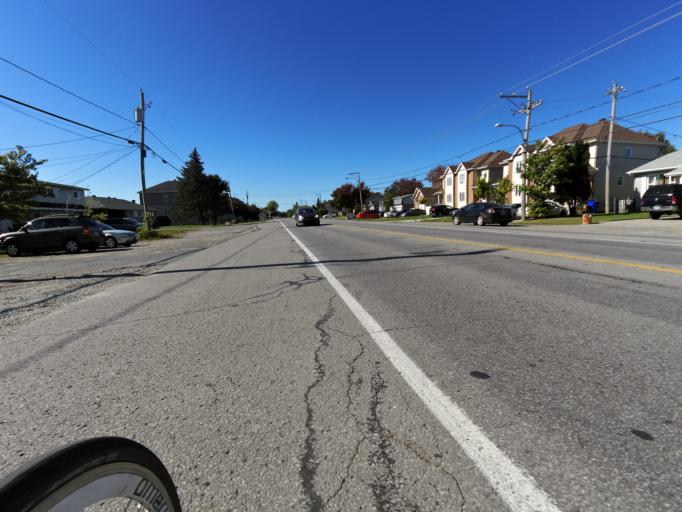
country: CA
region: Quebec
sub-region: Outaouais
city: Gatineau
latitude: 45.4988
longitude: -75.5701
